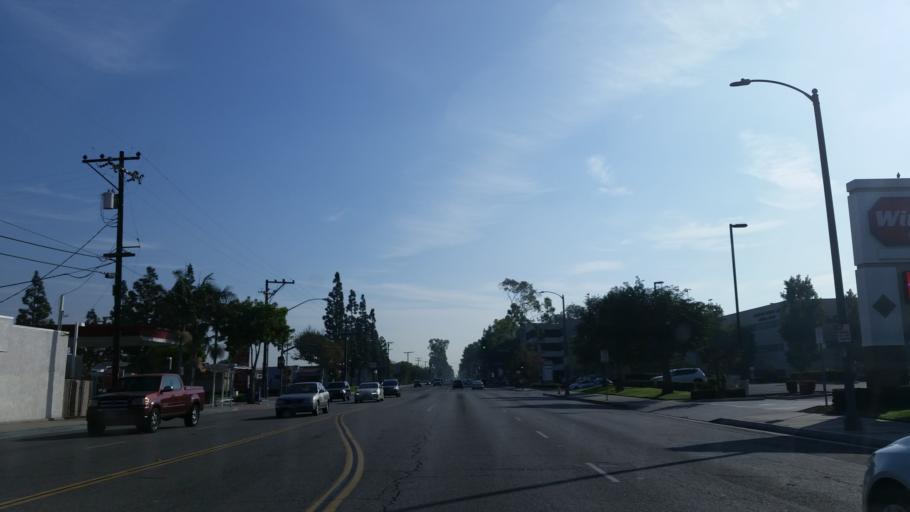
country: US
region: California
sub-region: Los Angeles County
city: Lakewood
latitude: 33.8602
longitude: -118.1523
